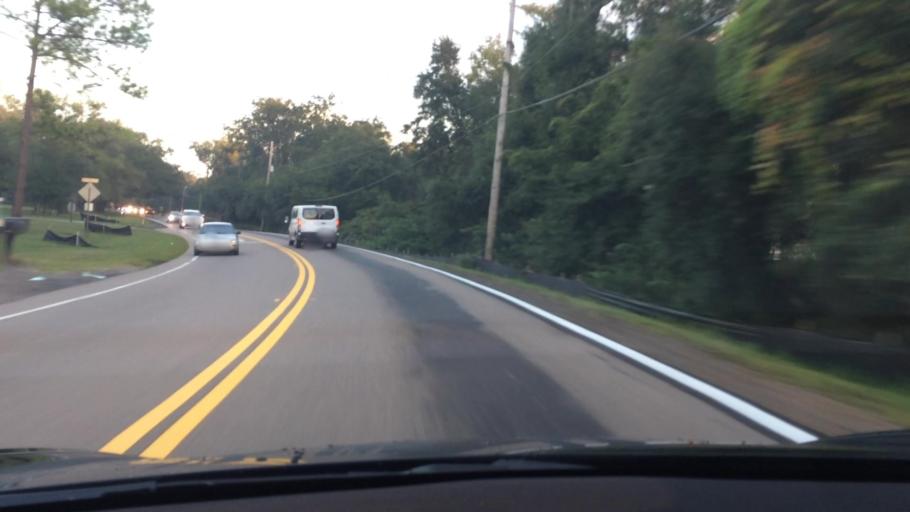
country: US
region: Florida
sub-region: Hillsborough County
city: Citrus Park
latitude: 28.1060
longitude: -82.5791
